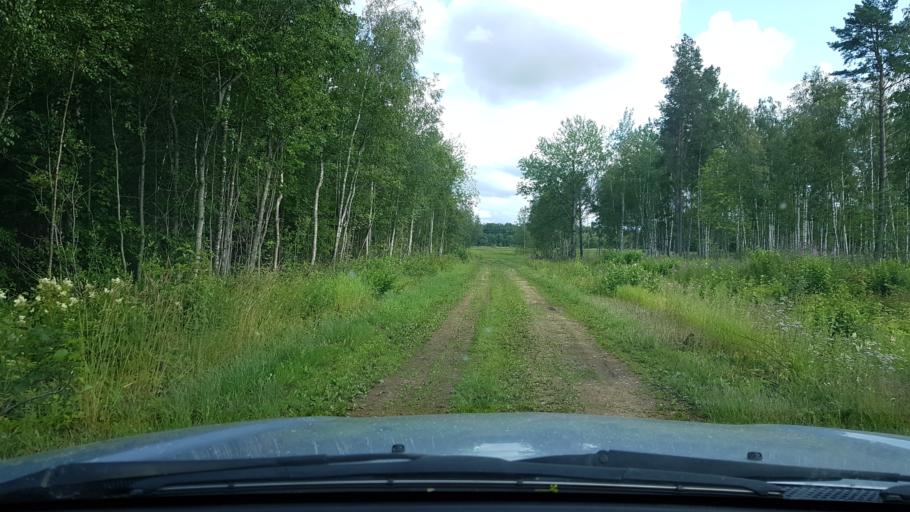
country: EE
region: Ida-Virumaa
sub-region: Narva-Joesuu linn
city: Narva-Joesuu
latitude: 59.3818
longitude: 27.9566
